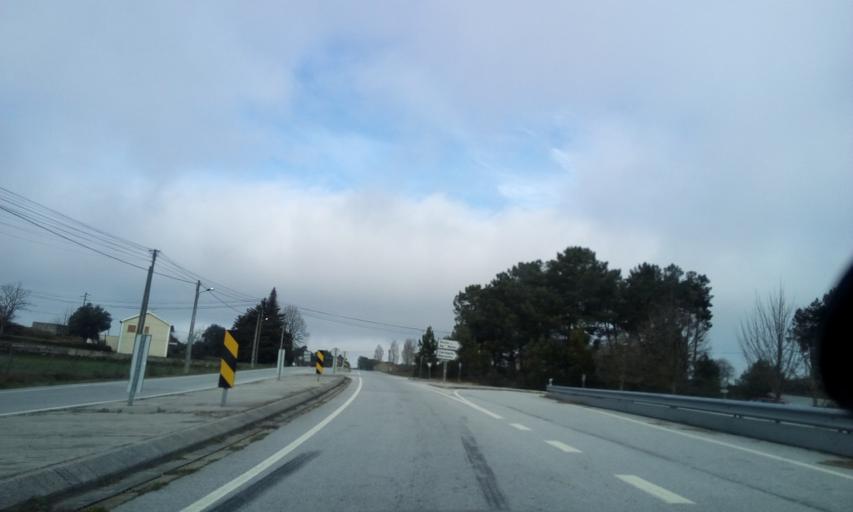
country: PT
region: Guarda
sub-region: Aguiar da Beira
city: Aguiar da Beira
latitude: 40.7889
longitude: -7.5044
